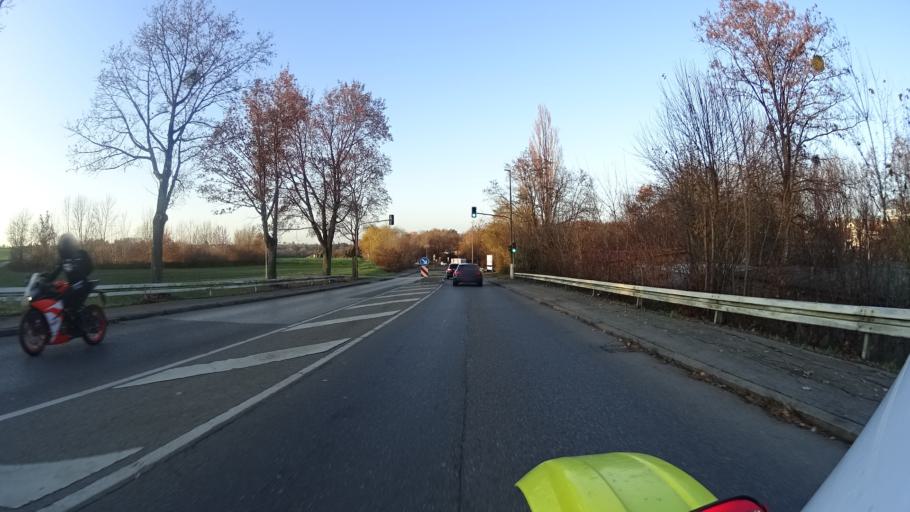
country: DE
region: Baden-Wuerttemberg
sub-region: Regierungsbezirk Stuttgart
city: Schlat
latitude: 48.6697
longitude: 9.6921
